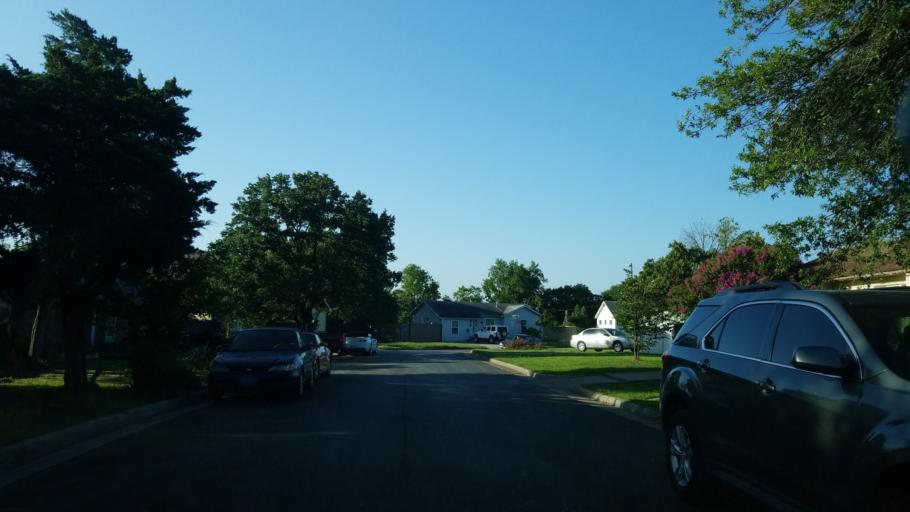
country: US
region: Texas
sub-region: Dallas County
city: Grand Prairie
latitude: 32.7533
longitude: -96.9504
